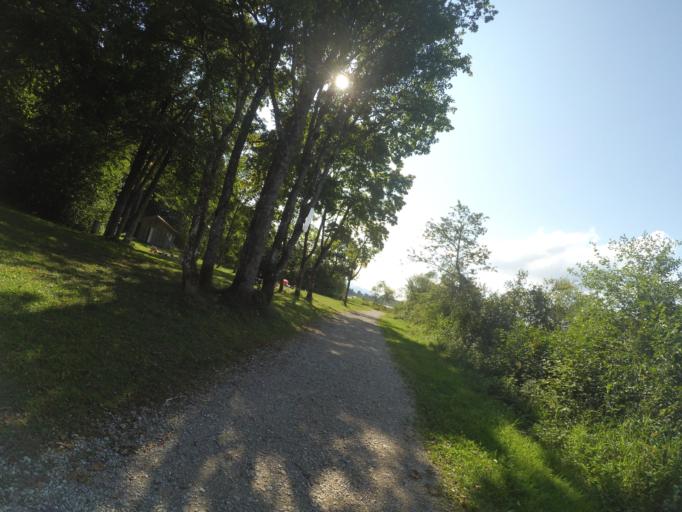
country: DE
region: Bavaria
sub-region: Swabia
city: Schwangau
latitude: 47.5940
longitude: 10.7753
